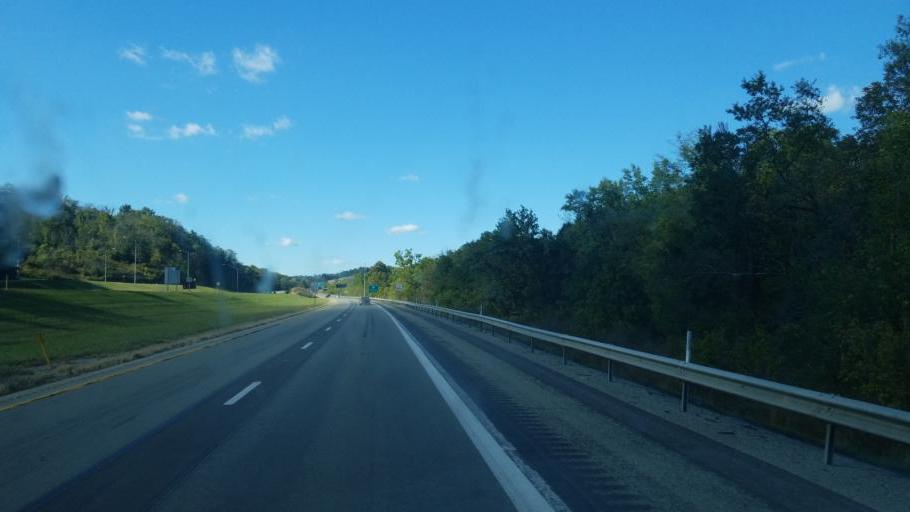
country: US
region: Pennsylvania
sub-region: Washington County
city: East Washington
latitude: 40.1202
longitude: -80.2047
